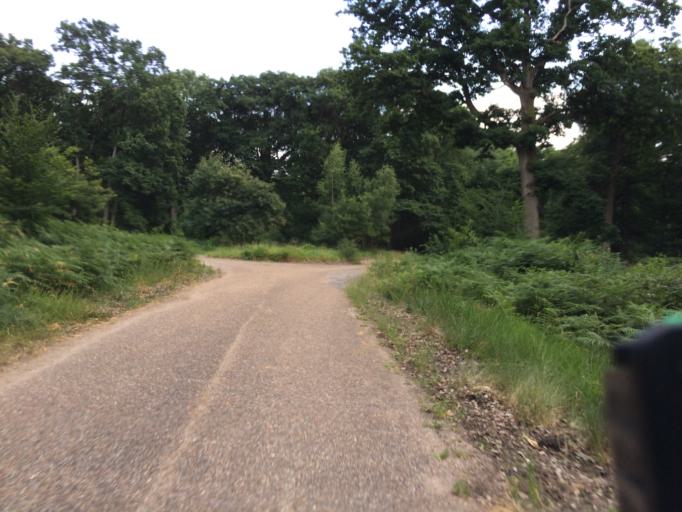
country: FR
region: Ile-de-France
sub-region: Departement de l'Essonne
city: Soisy-sur-Seine
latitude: 48.6689
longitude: 2.4446
